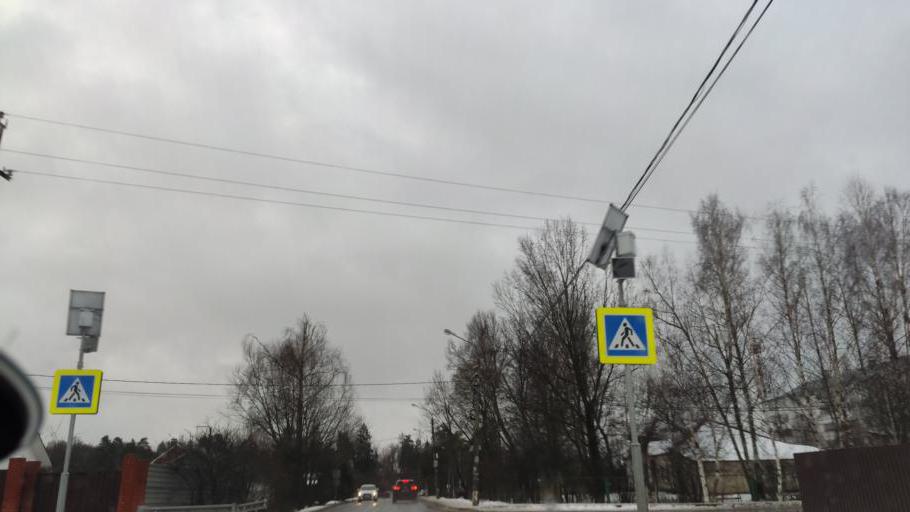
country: RU
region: Moskovskaya
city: Vatutinki
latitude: 55.4562
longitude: 37.3997
